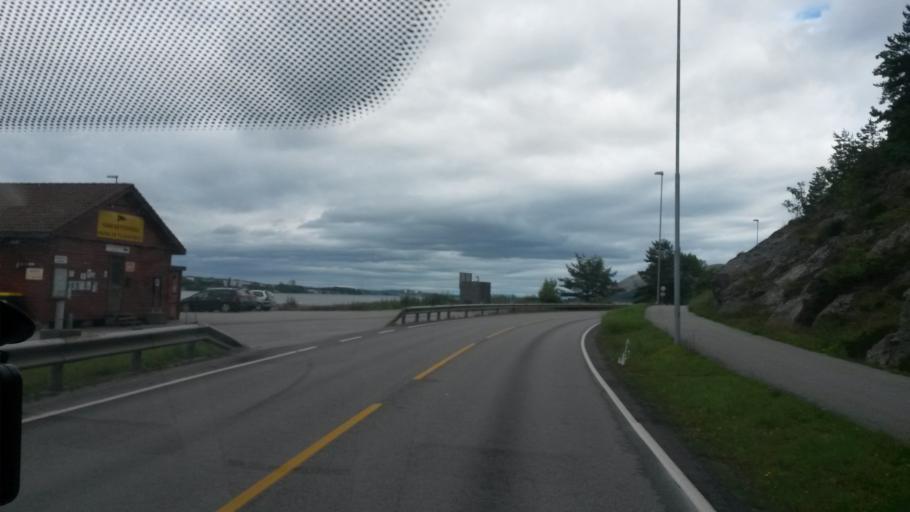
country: NO
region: Rogaland
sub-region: Sandnes
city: Sandnes
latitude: 58.8658
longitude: 5.7564
